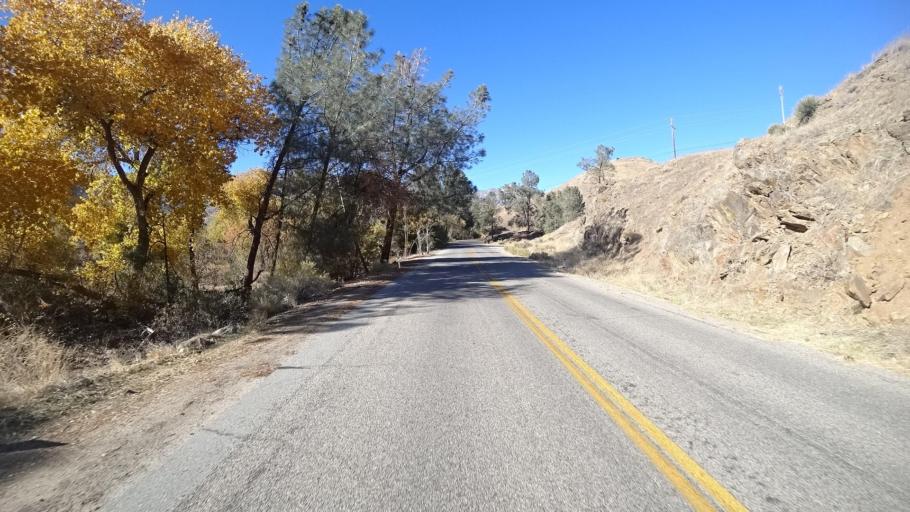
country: US
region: California
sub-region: Kern County
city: Kernville
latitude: 35.7807
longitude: -118.4393
